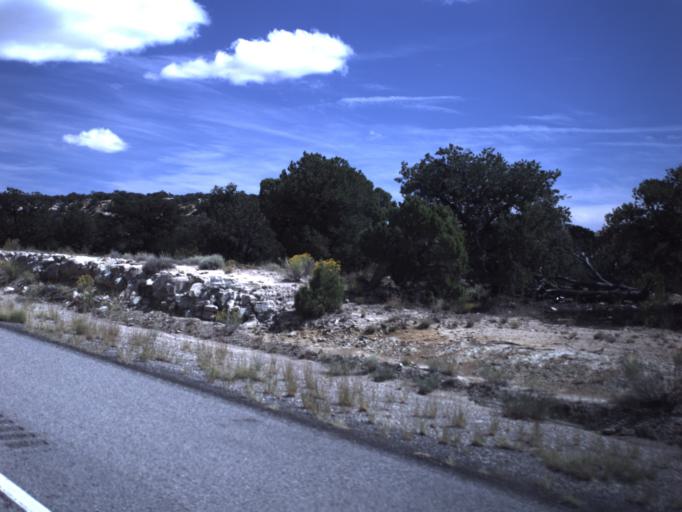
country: US
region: Utah
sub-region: Emery County
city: Ferron
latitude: 38.8587
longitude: -110.8331
